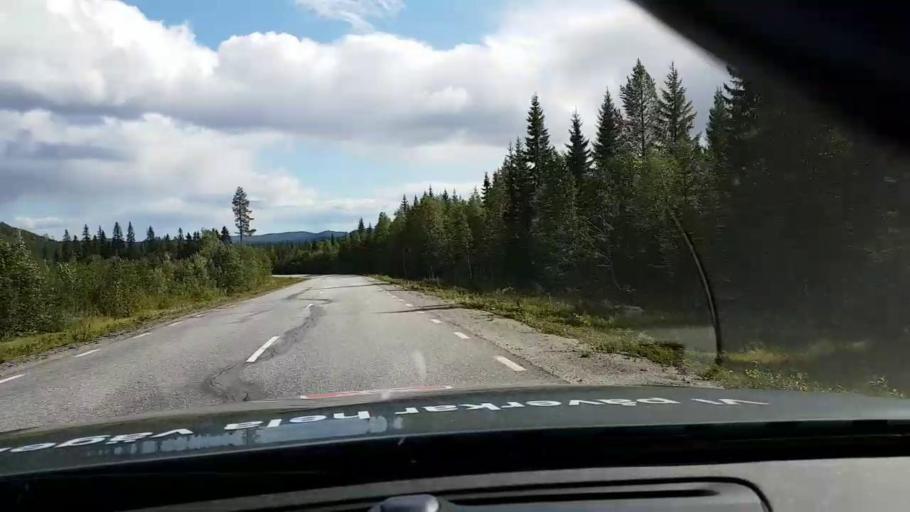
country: SE
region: Vaesternorrland
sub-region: OErnskoeldsviks Kommun
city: Bredbyn
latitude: 63.7649
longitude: 17.6863
